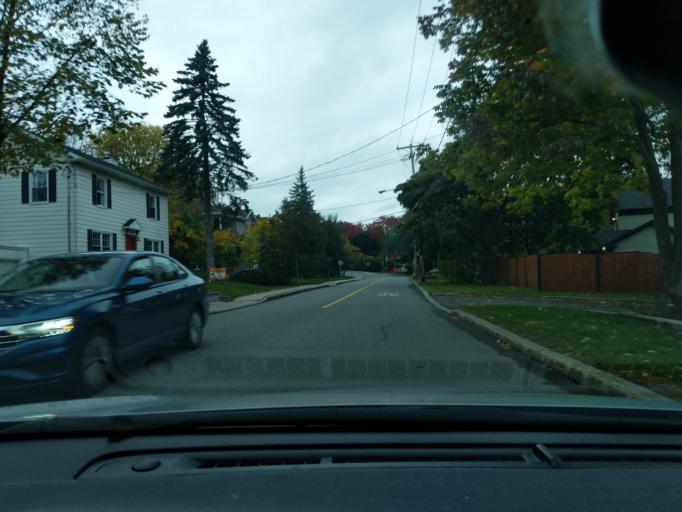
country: CA
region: Quebec
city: Quebec
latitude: 46.7671
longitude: -71.2666
